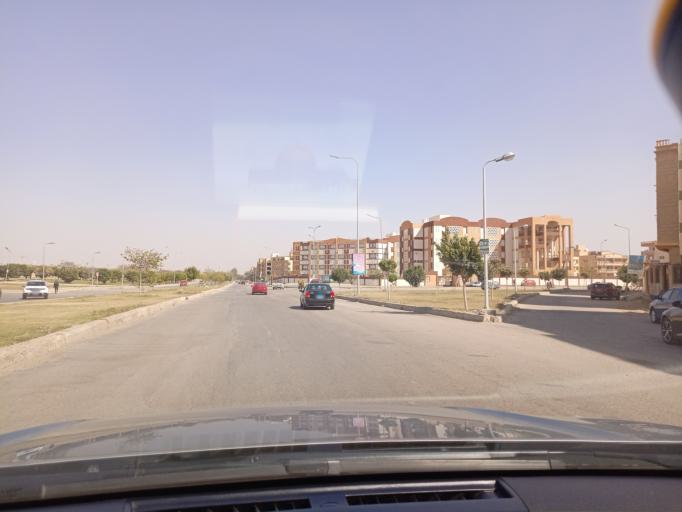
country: EG
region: Muhafazat al Qalyubiyah
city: Al Khankah
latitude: 30.2274
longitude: 31.4471
